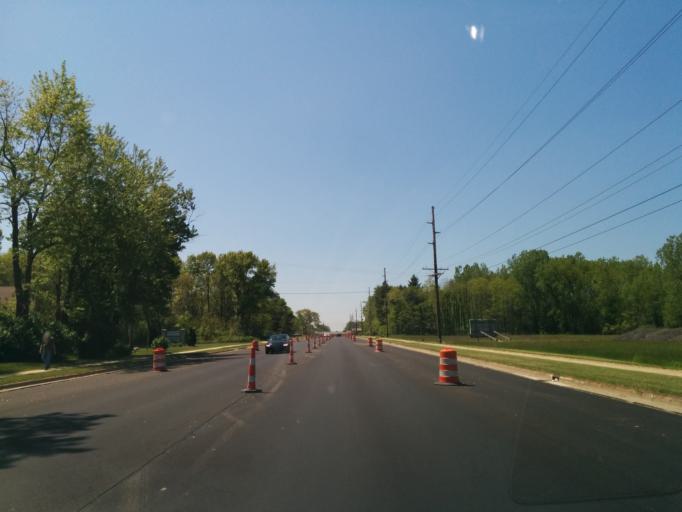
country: US
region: Michigan
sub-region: Berrien County
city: Bridgman
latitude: 41.9360
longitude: -86.5679
